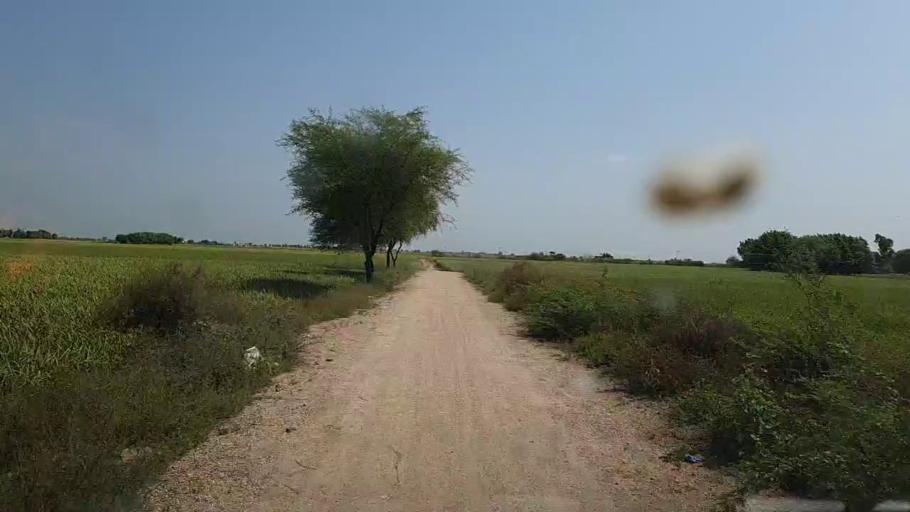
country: PK
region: Sindh
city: Kario
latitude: 24.6331
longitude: 68.5435
